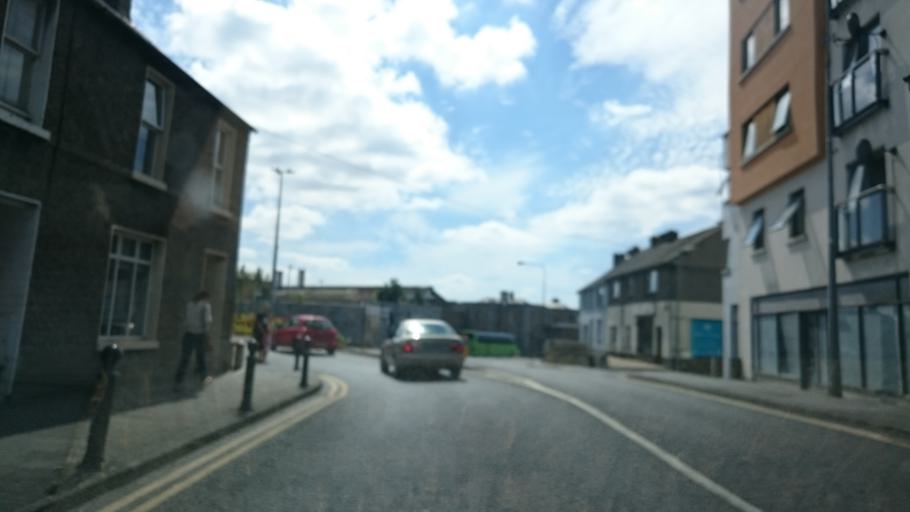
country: IE
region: Leinster
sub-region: Kilkenny
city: Kilkenny
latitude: 52.6564
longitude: -7.2456
